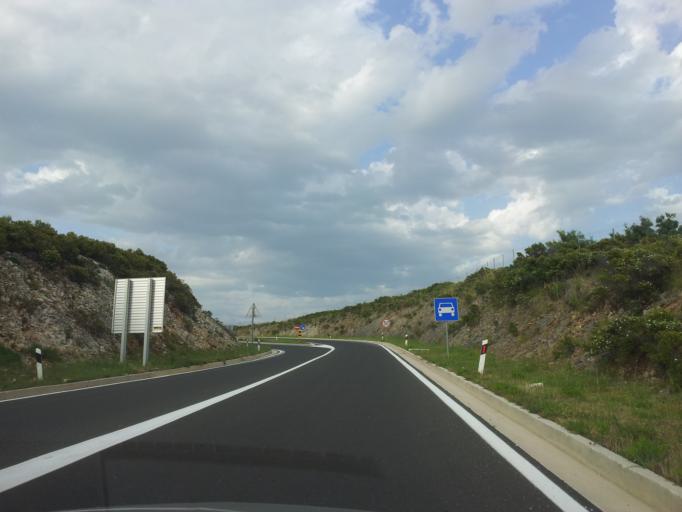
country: HR
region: Zadarska
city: Sukosan
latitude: 44.0702
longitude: 15.3399
